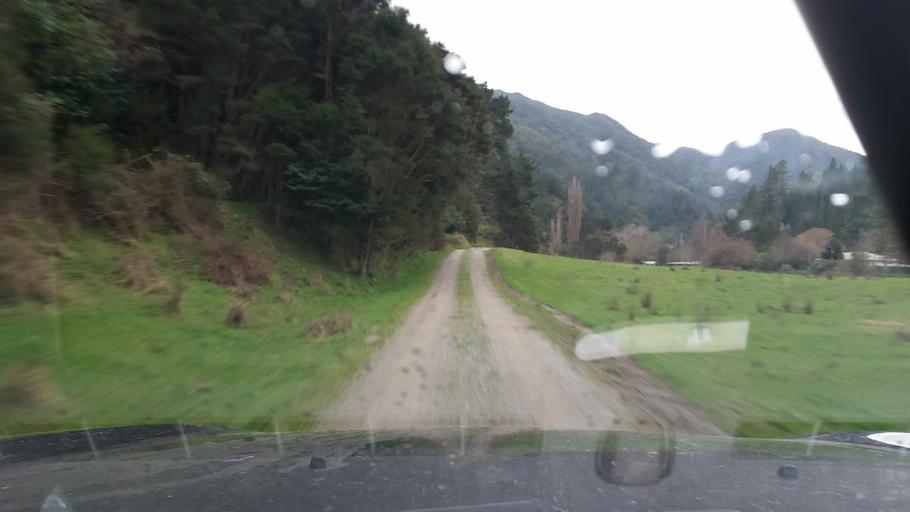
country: NZ
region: Marlborough
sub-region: Marlborough District
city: Blenheim
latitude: -41.3886
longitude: 173.8488
